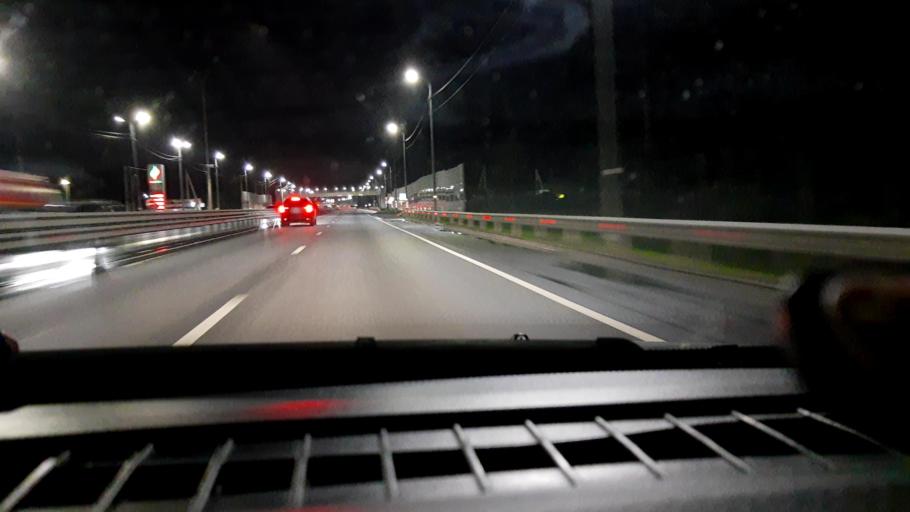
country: RU
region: Moskovskaya
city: Malaya Dubna
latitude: 55.8792
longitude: 38.9752
